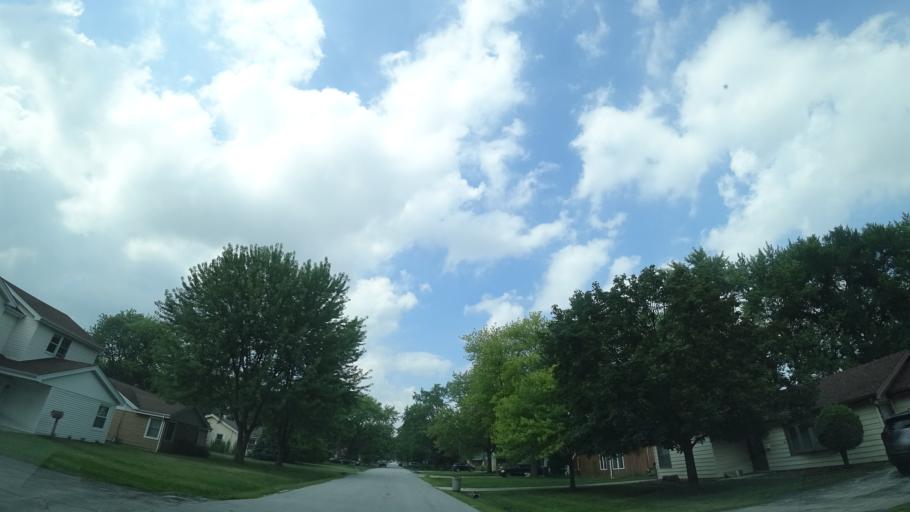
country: US
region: Illinois
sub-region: Cook County
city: Worth
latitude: 41.6806
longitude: -87.7821
